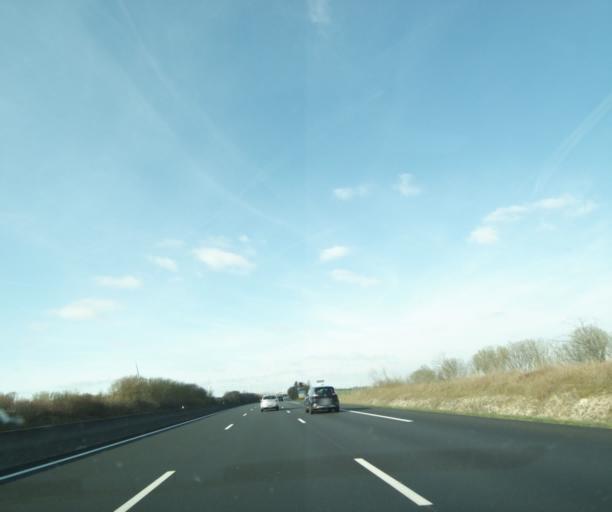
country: FR
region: Centre
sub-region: Departement d'Eure-et-Loir
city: Janville
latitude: 48.2577
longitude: 1.8517
